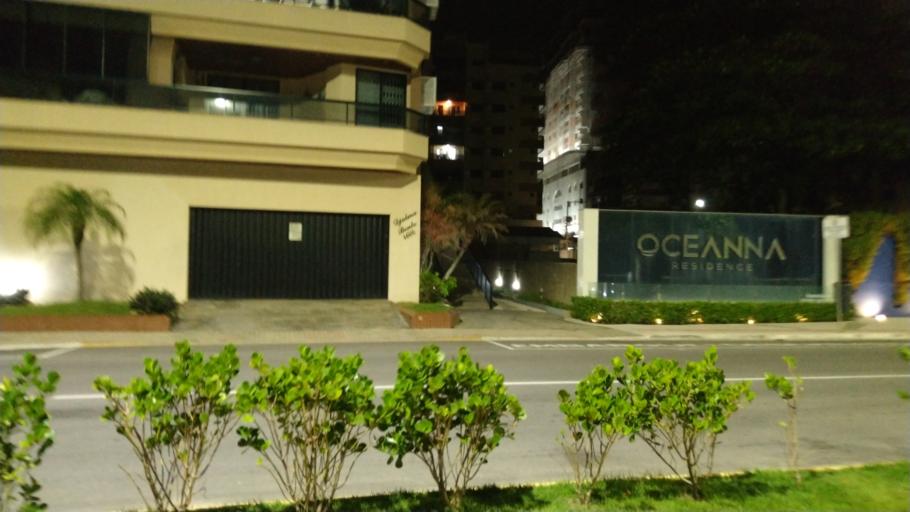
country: BR
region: Santa Catarina
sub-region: Itapema
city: Itapema
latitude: -27.0994
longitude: -48.6140
